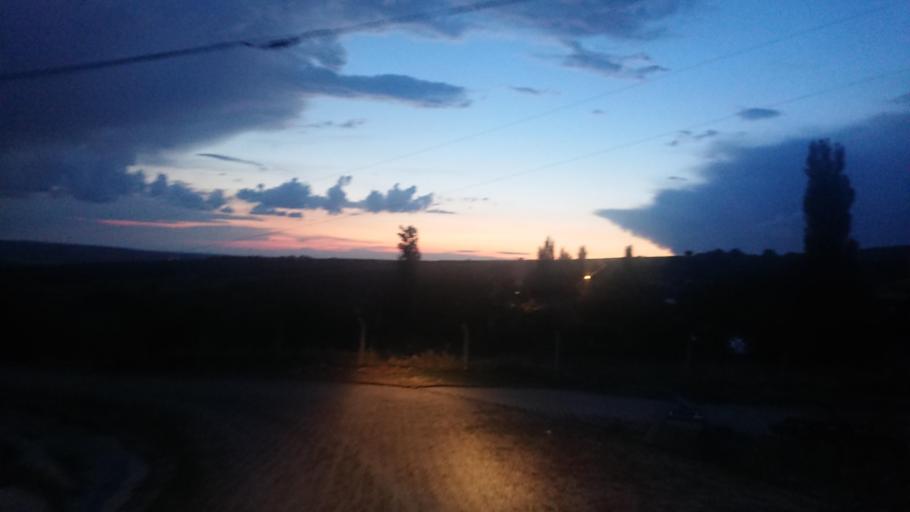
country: TR
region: Aksaray
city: Ortakoy
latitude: 38.6344
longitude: 34.0159
